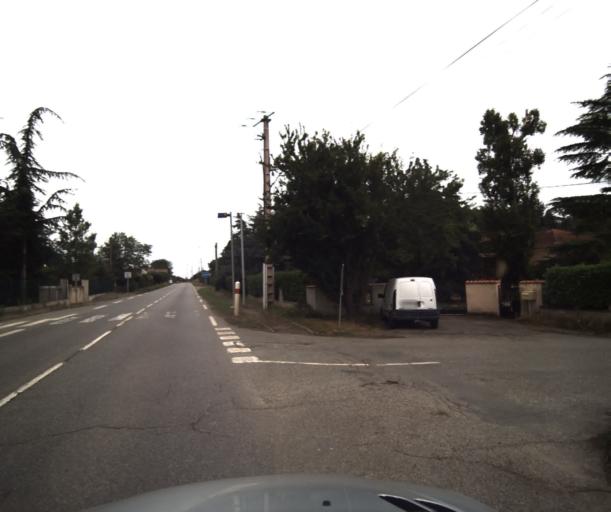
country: FR
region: Midi-Pyrenees
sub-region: Departement de la Haute-Garonne
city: Labarthe-sur-Leze
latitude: 43.4676
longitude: 1.3978
